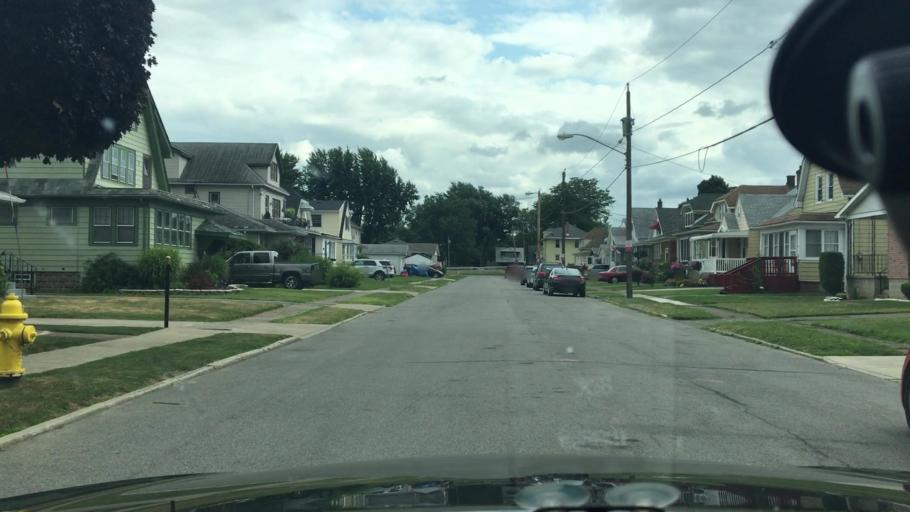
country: US
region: New York
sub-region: Erie County
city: Lackawanna
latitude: 42.8315
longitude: -78.8187
